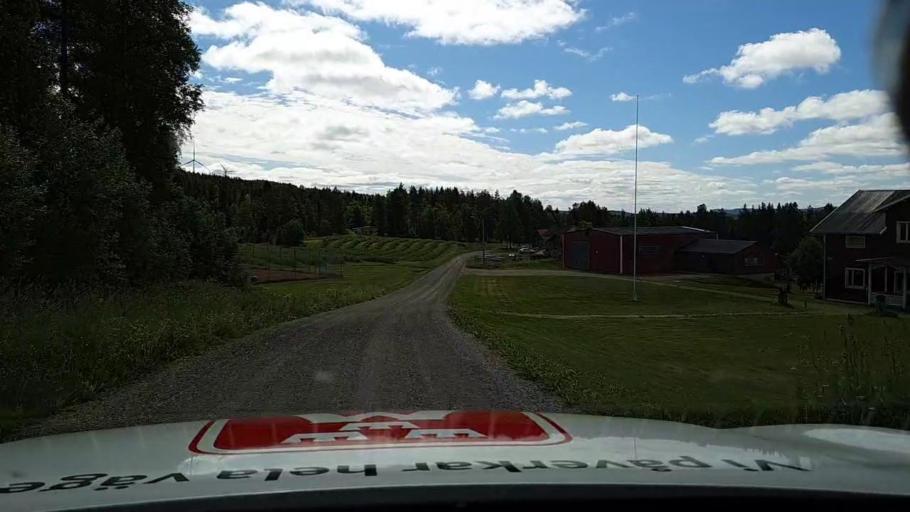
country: SE
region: Jaemtland
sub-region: Braecke Kommun
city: Braecke
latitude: 62.7644
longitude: 15.4983
